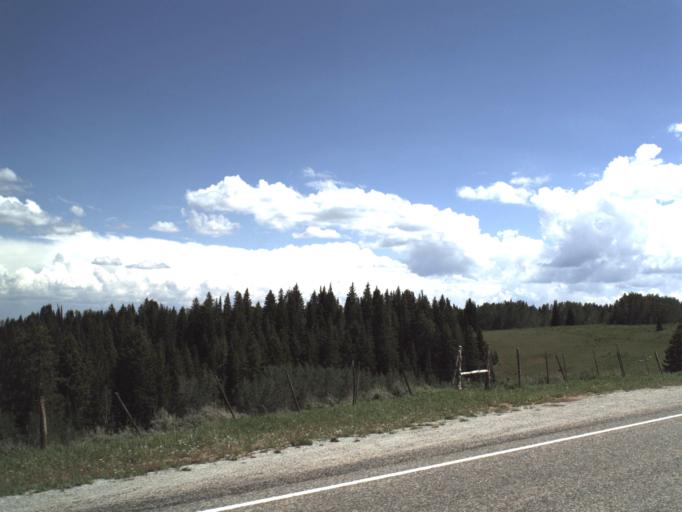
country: US
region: Utah
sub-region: Weber County
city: Wolf Creek
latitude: 41.4482
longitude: -111.5028
